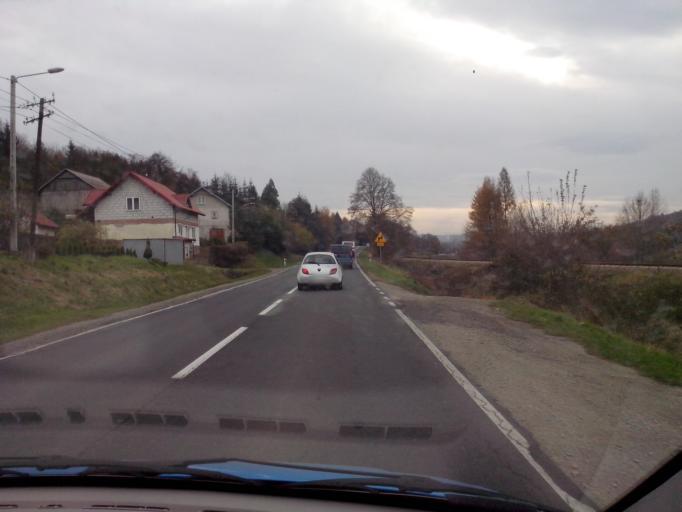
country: PL
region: Subcarpathian Voivodeship
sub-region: Powiat strzyzowski
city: Strzyzow
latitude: 49.8866
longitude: 21.8254
